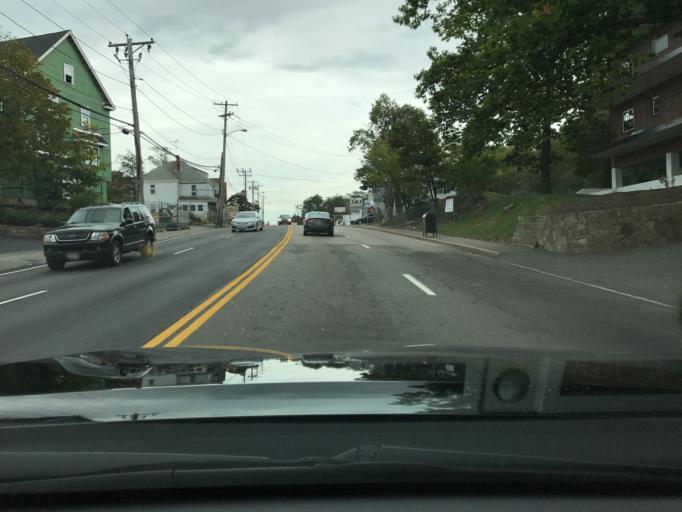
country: US
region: Massachusetts
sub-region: Norfolk County
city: Quincy
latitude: 42.2425
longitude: -70.9954
